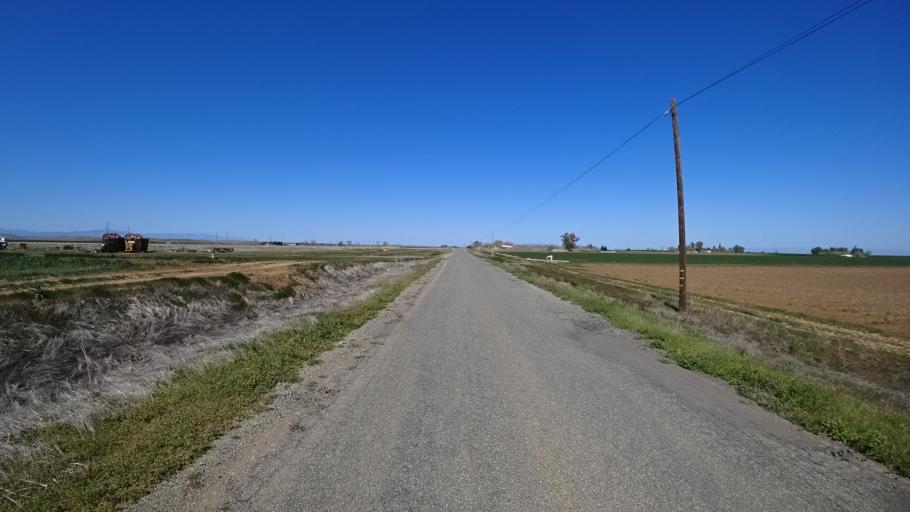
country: US
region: California
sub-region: Glenn County
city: Willows
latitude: 39.5179
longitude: -122.2775
